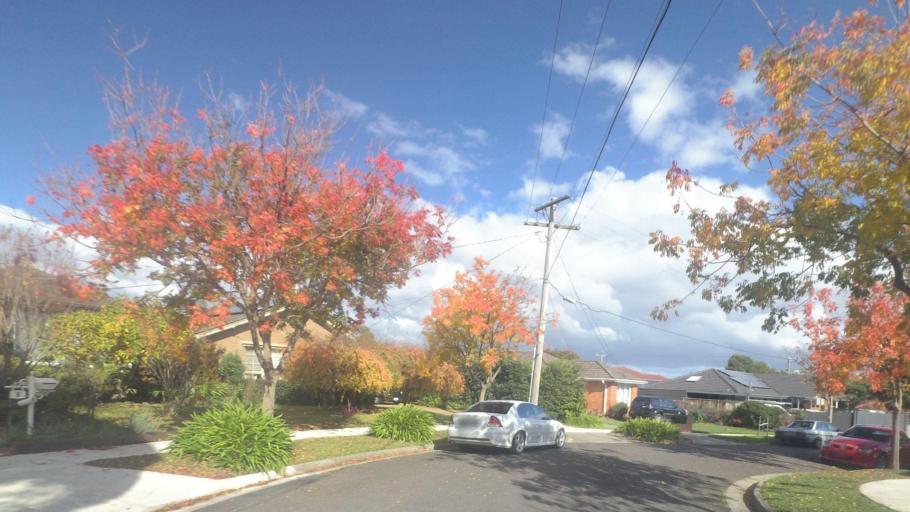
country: AU
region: Victoria
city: Forest Hill
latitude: -37.8387
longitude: 145.1846
